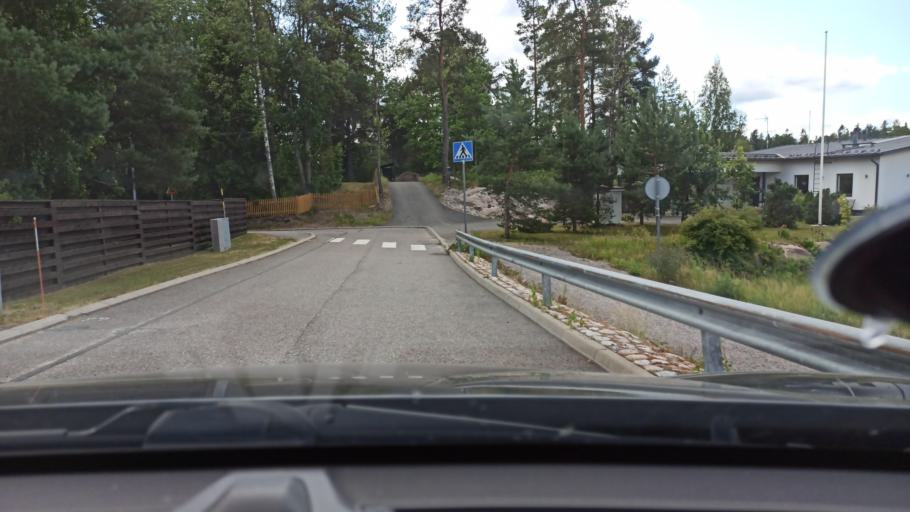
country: FI
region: Uusimaa
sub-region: Helsinki
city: Kirkkonummi
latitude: 60.2755
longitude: 24.4131
